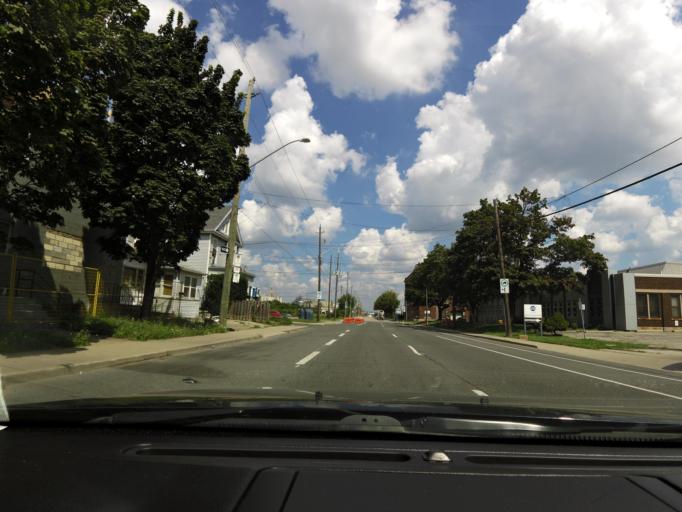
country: CA
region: Ontario
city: Hamilton
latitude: 43.2650
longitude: -79.8516
